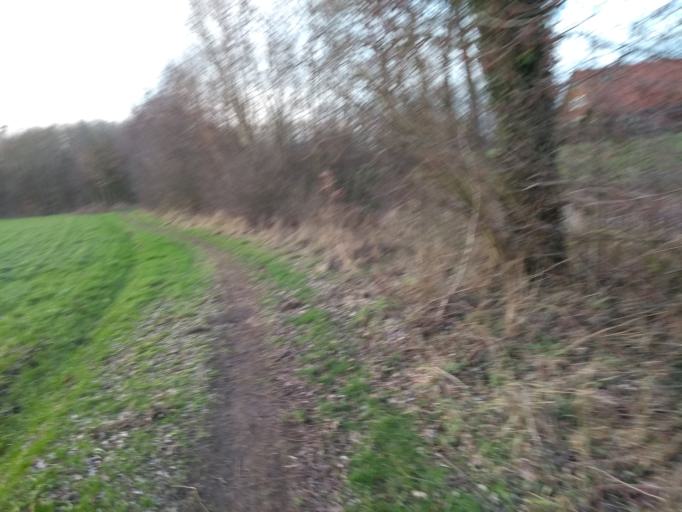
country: NL
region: Overijssel
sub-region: Gemeente Borne
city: Borne
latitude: 52.3289
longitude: 6.7447
